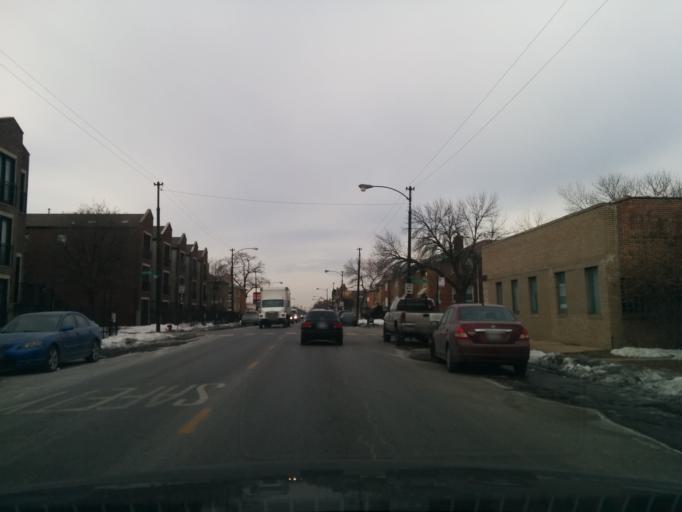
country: US
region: Illinois
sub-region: Cook County
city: Elmwood Park
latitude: 41.9382
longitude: -87.7915
